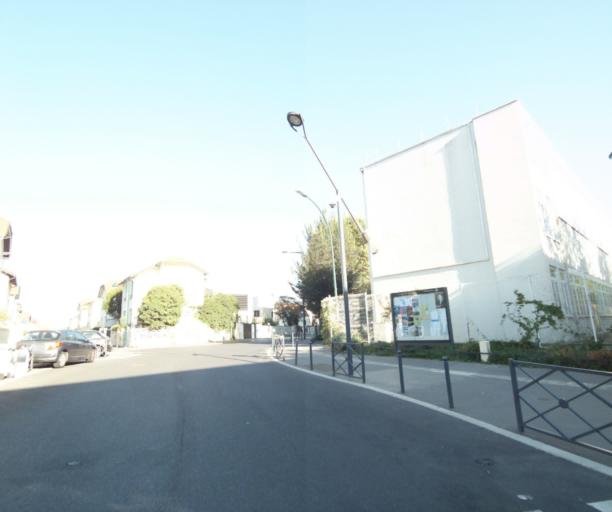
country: FR
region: Ile-de-France
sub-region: Departement des Hauts-de-Seine
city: Villeneuve-la-Garenne
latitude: 48.9330
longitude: 2.3294
